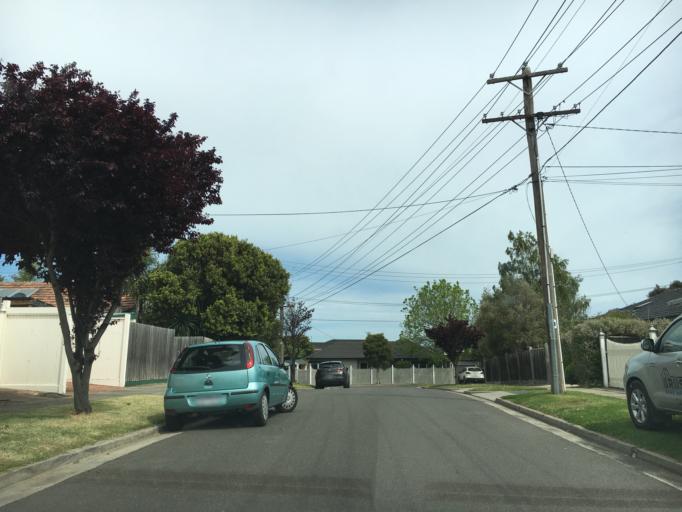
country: AU
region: Victoria
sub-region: Monash
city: Chadstone
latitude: -37.8879
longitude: 145.1037
